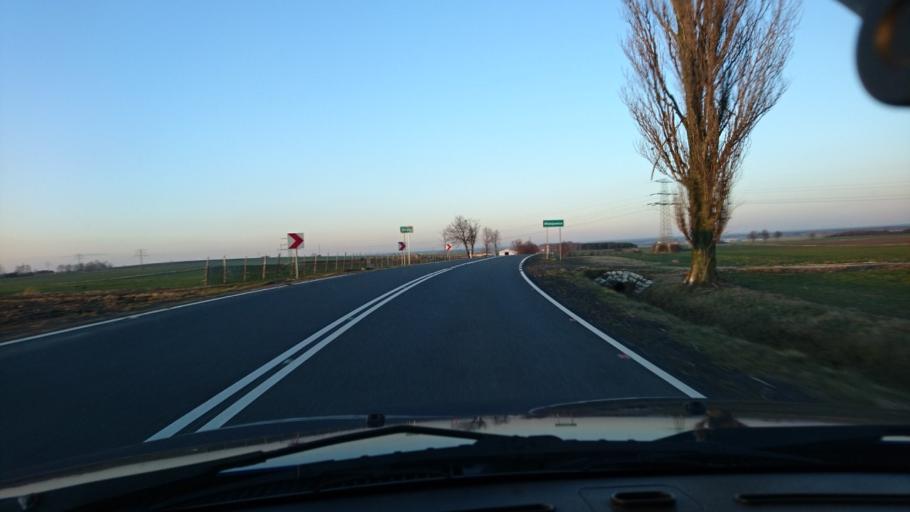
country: PL
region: Silesian Voivodeship
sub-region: Powiat gliwicki
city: Wielowies
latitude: 50.4855
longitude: 18.6046
